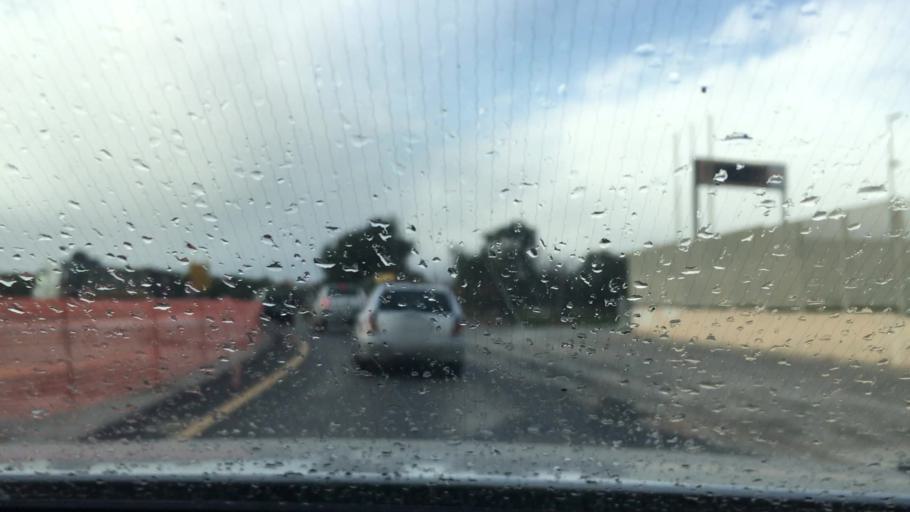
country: IT
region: Apulia
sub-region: Provincia di Bari
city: Palo del Colle
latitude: 41.0672
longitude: 16.7281
